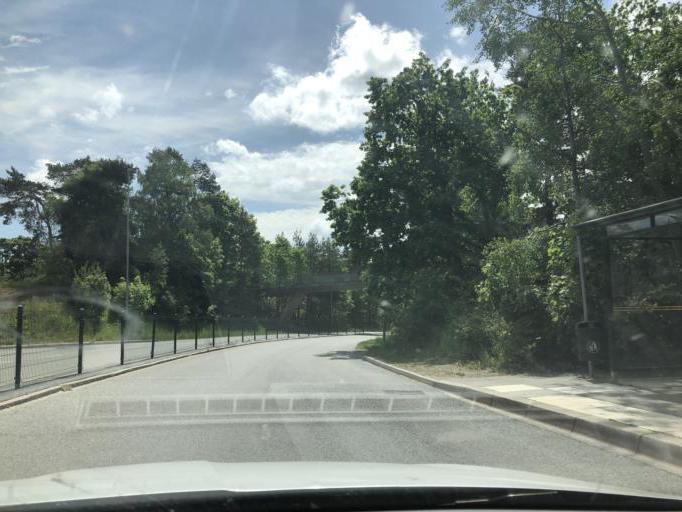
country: SE
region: Stockholm
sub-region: Botkyrka Kommun
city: Fittja
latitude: 59.2421
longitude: 17.8545
